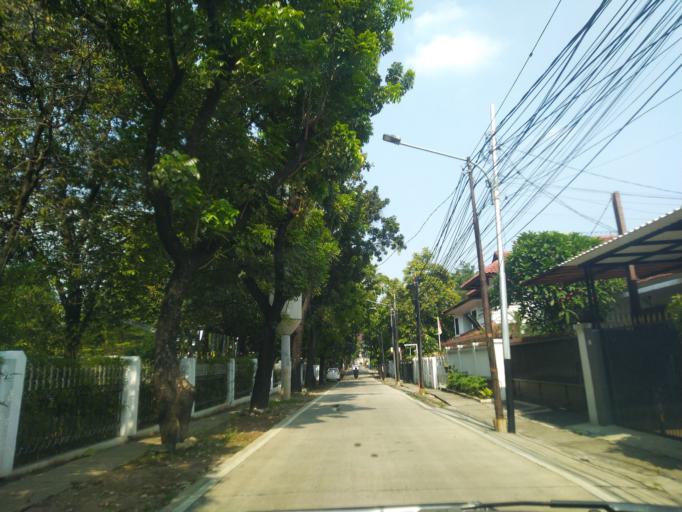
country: ID
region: Jakarta Raya
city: Jakarta
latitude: -6.2368
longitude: 106.7947
